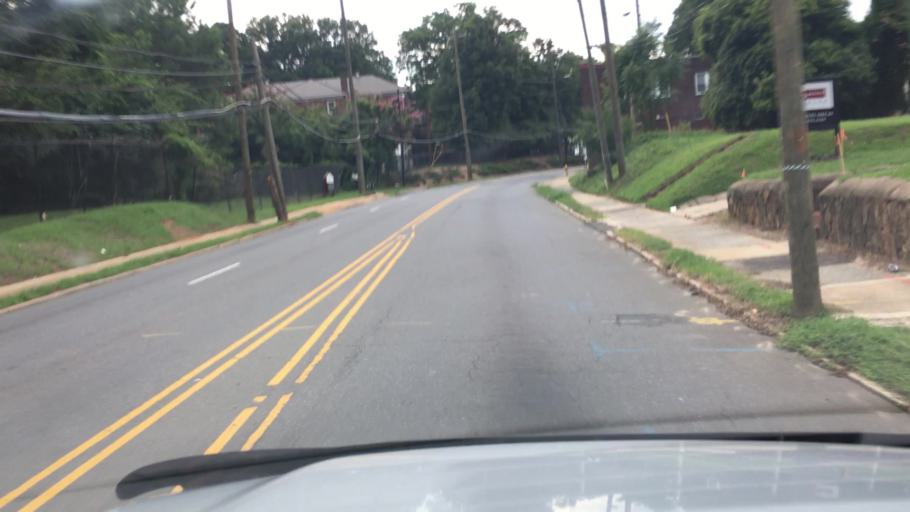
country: US
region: North Carolina
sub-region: Mecklenburg County
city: Charlotte
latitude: 35.2462
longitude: -80.8569
